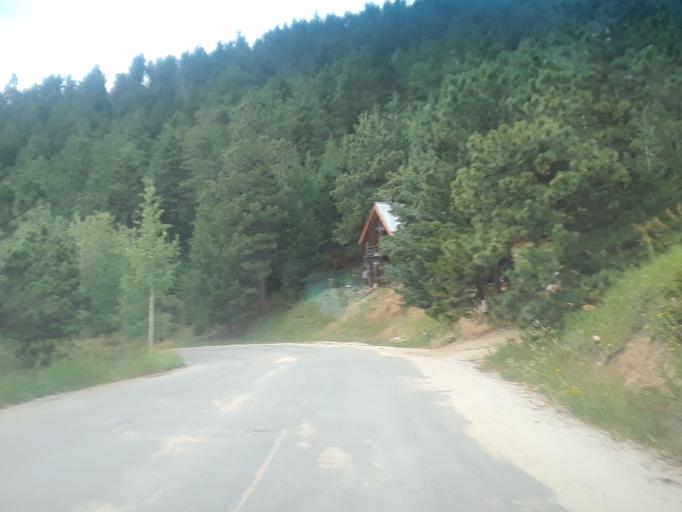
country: US
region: Colorado
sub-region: Boulder County
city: Boulder
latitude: 40.0715
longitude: -105.3848
